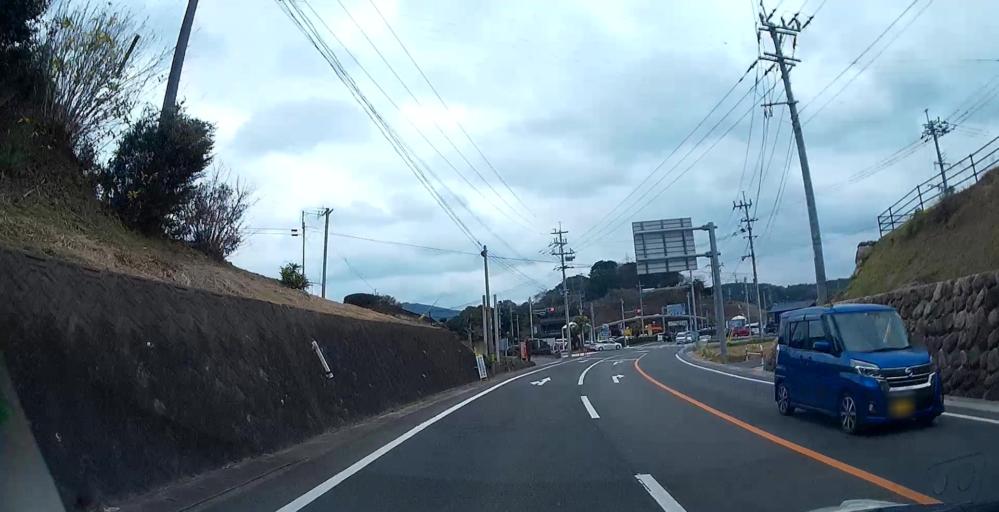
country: JP
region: Kagoshima
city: Akune
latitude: 32.1091
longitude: 130.1693
